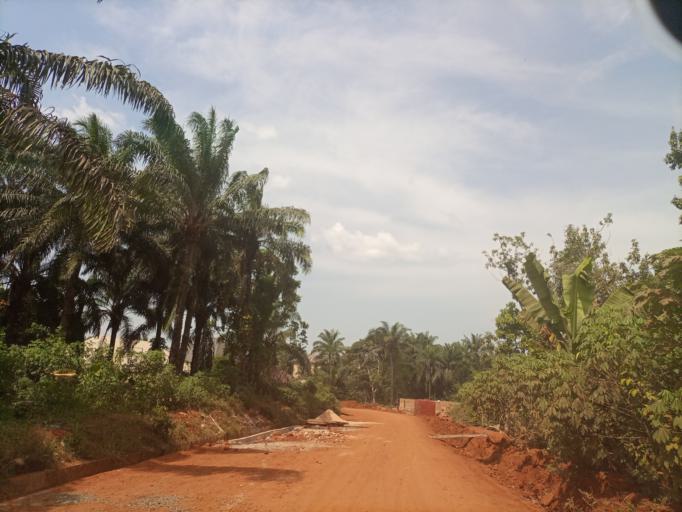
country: NG
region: Enugu
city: Obollo-Afor
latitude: 6.8678
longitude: 7.4723
